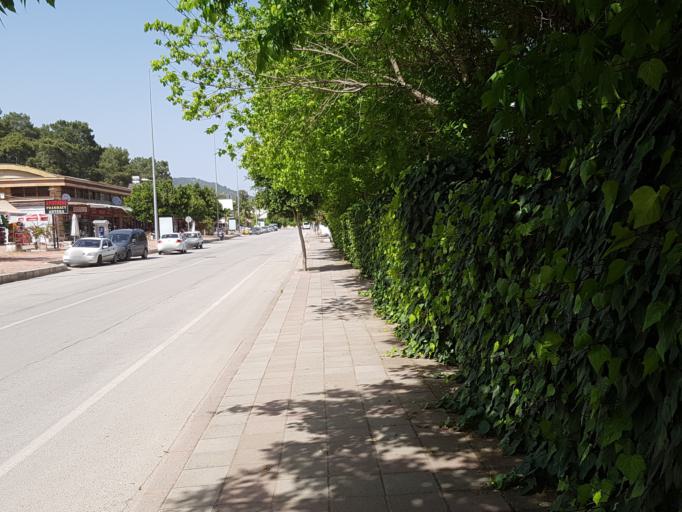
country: TR
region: Antalya
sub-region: Kemer
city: Goeynuek
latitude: 36.6552
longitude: 30.5546
